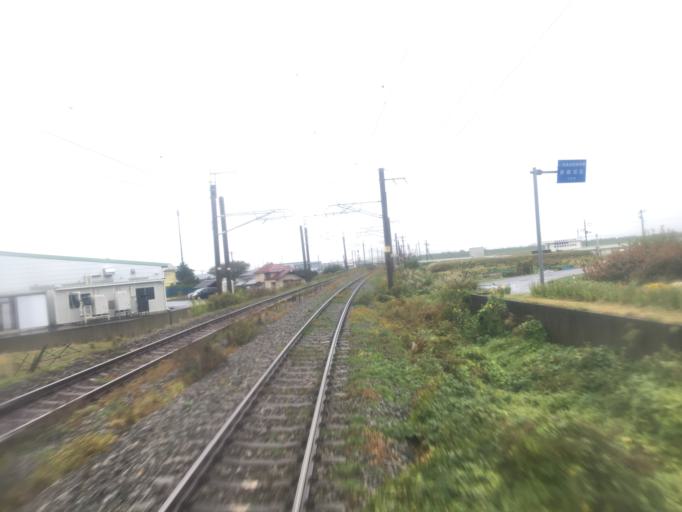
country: JP
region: Yamagata
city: Sakata
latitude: 38.8904
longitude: 139.9099
